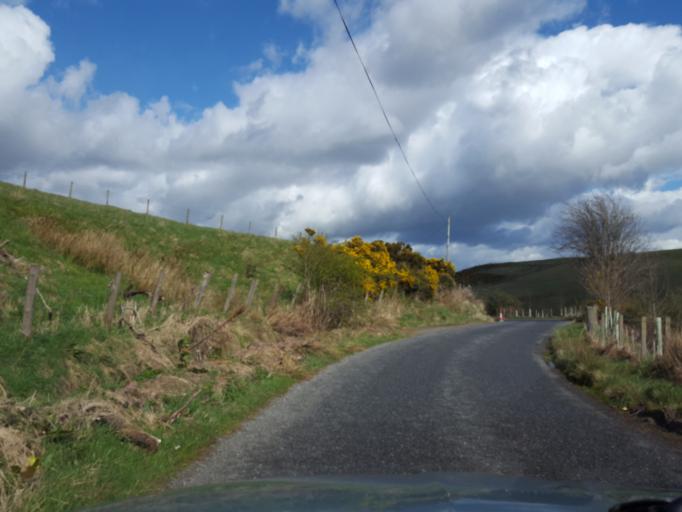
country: GB
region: Scotland
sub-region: Perth and Kinross
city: Auchterarder
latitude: 56.2852
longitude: -3.5799
